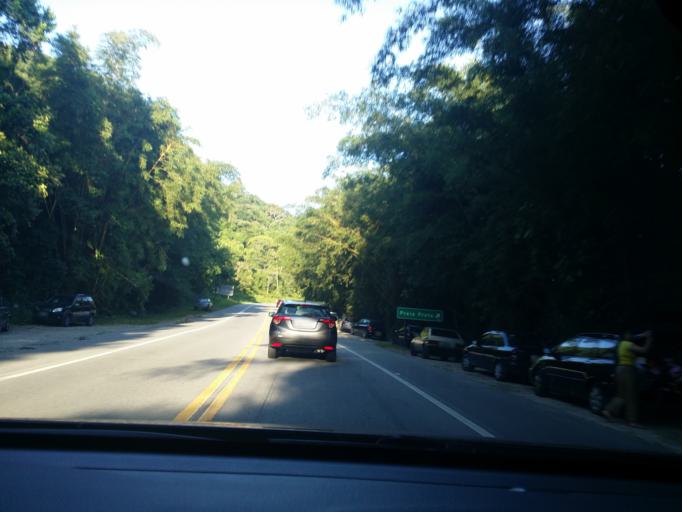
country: BR
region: Sao Paulo
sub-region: Sao Sebastiao
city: Sao Sebastiao
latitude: -23.7708
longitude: -45.7124
